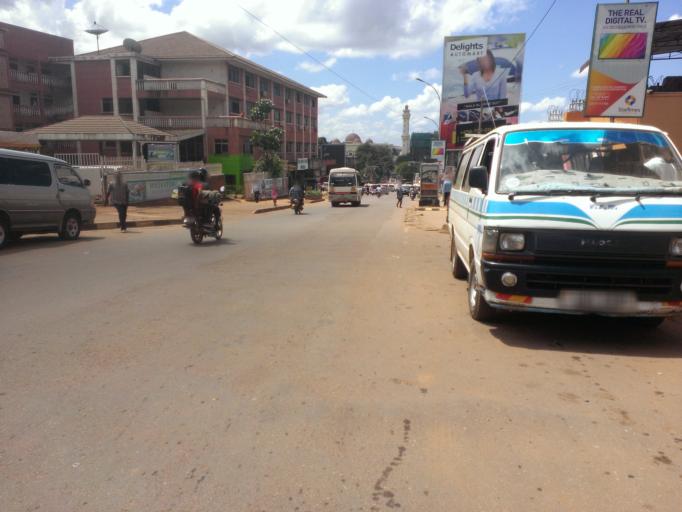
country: UG
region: Central Region
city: Kampala Central Division
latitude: 0.3145
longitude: 32.5635
